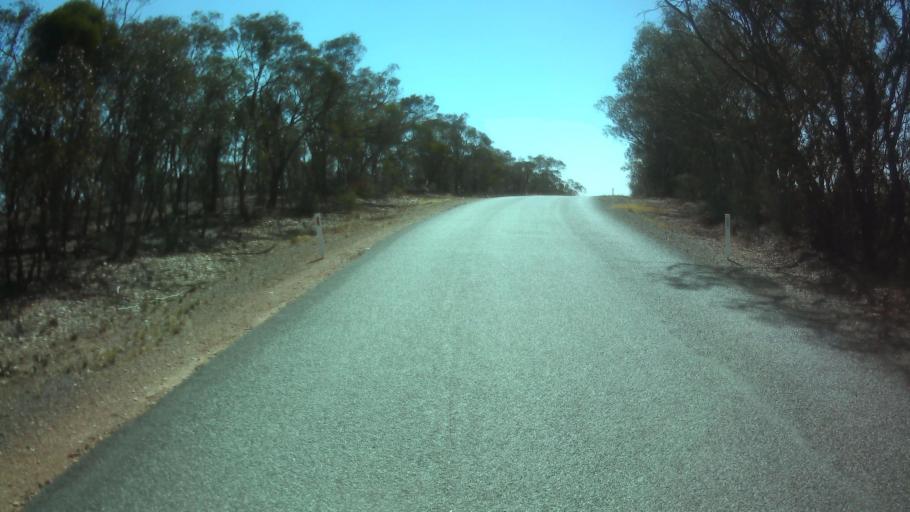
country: AU
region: New South Wales
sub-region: Weddin
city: Grenfell
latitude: -33.7558
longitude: 147.8267
